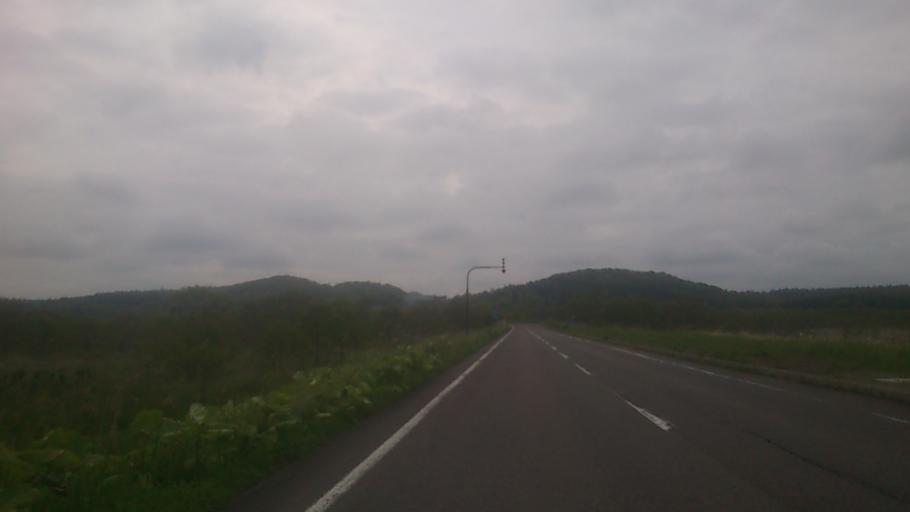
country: JP
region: Hokkaido
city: Nemuro
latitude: 43.0848
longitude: 145.0700
